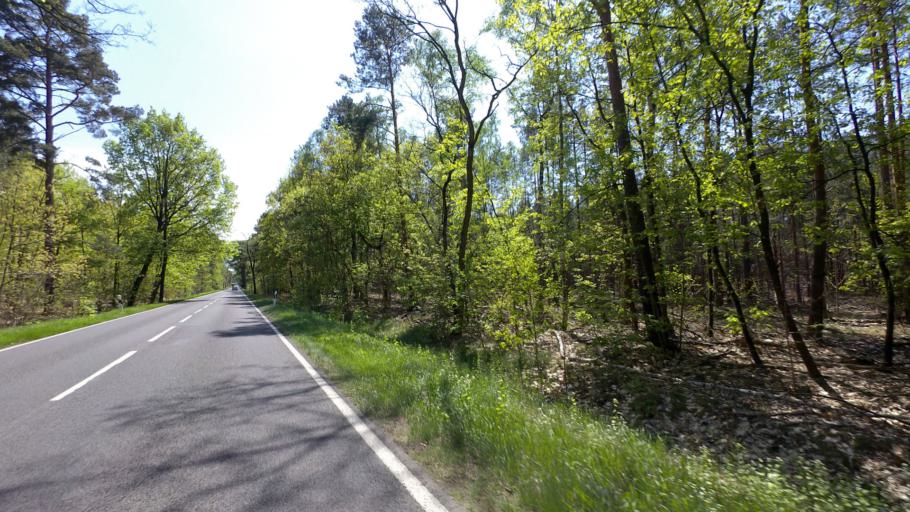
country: DE
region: Brandenburg
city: Gross Koris
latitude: 52.1821
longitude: 13.7086
